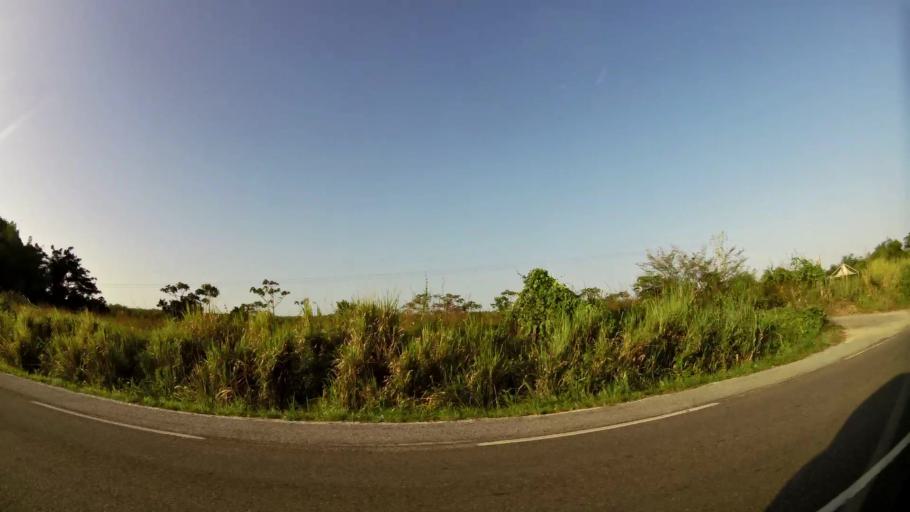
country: GF
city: Macouria
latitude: 5.0165
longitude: -52.4770
